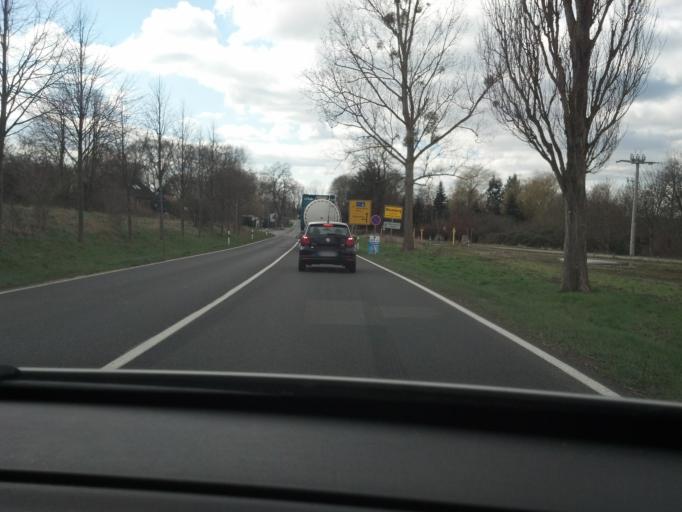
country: DE
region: Mecklenburg-Vorpommern
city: Wesenberg
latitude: 53.2809
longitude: 12.9895
